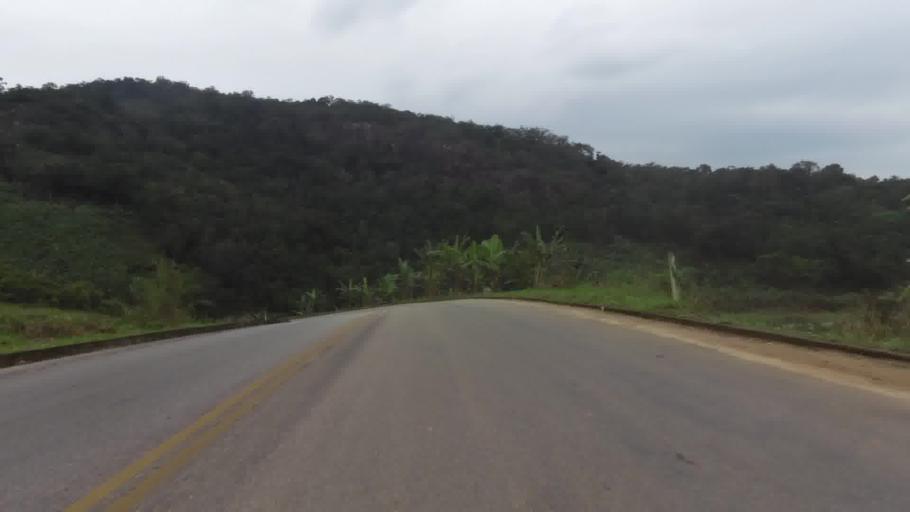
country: BR
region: Espirito Santo
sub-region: Iconha
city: Iconha
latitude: -20.7848
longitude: -40.8141
